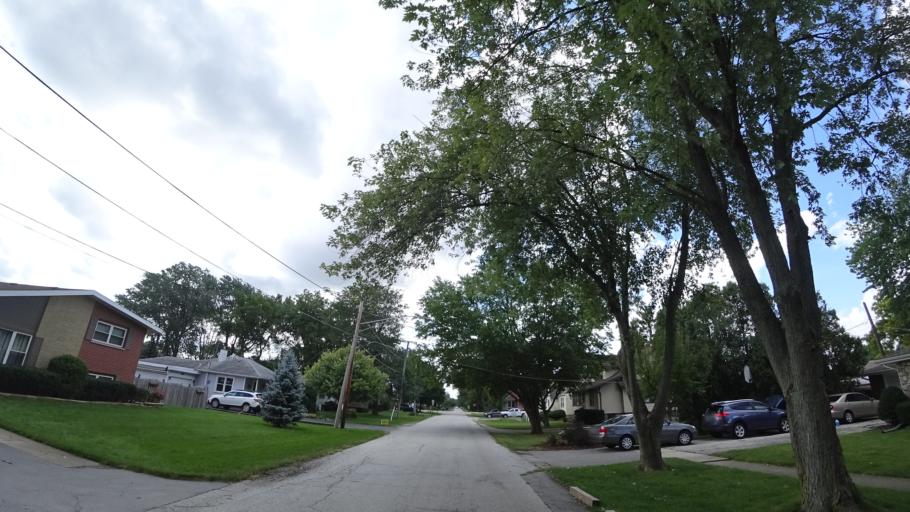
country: US
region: Illinois
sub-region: Cook County
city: Tinley Park
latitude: 41.5744
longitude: -87.7770
